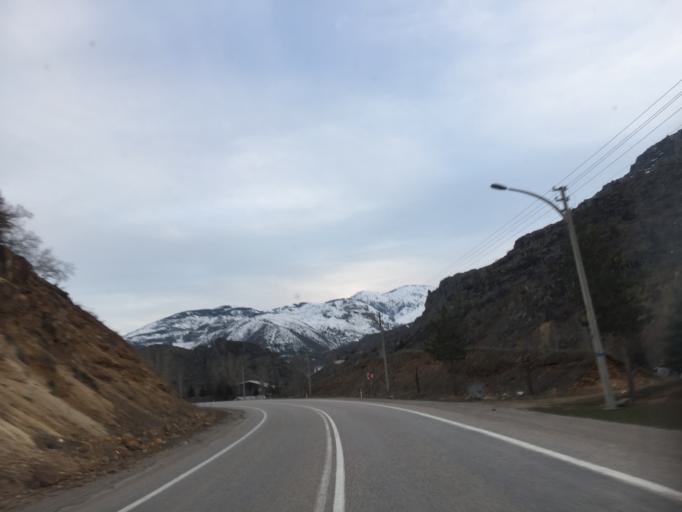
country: TR
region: Gumushane
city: Gumushkhane
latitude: 40.4777
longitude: 39.4614
